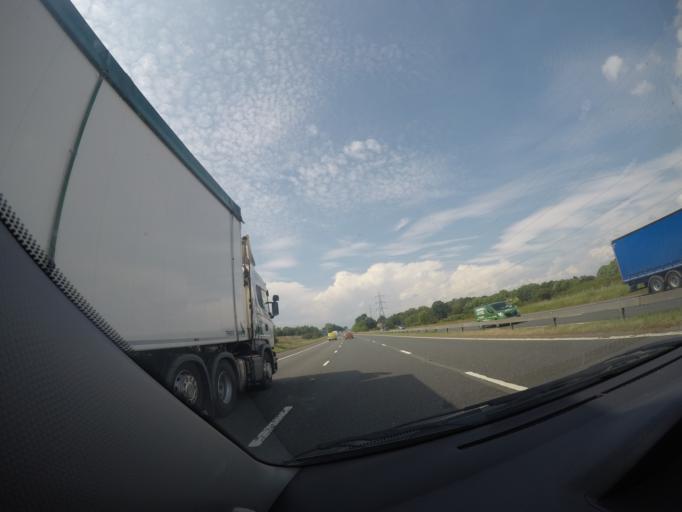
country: GB
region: England
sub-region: Cumbria
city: Scotby
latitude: 54.8748
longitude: -2.8776
